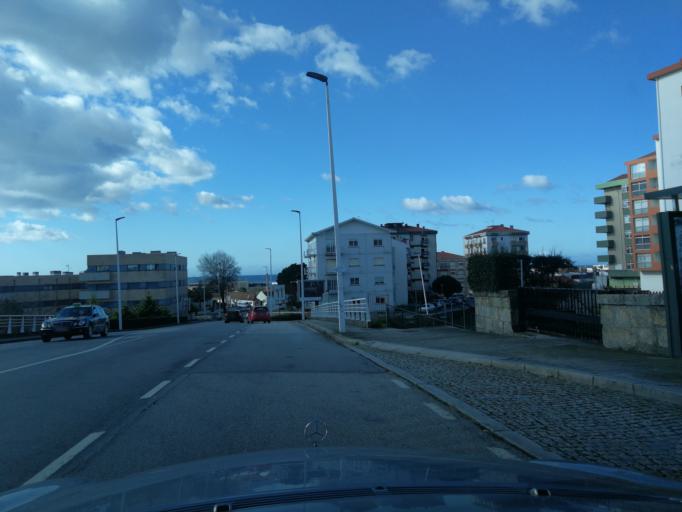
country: PT
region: Viana do Castelo
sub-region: Viana do Castelo
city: Viana do Castelo
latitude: 41.6947
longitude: -8.8392
